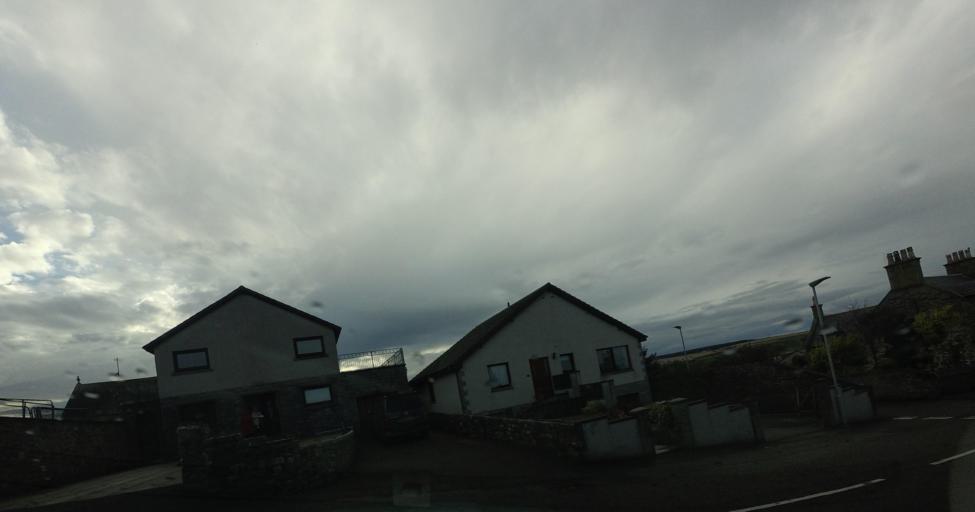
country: GB
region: Scotland
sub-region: Moray
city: Cullen
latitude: 57.6928
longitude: -2.8196
